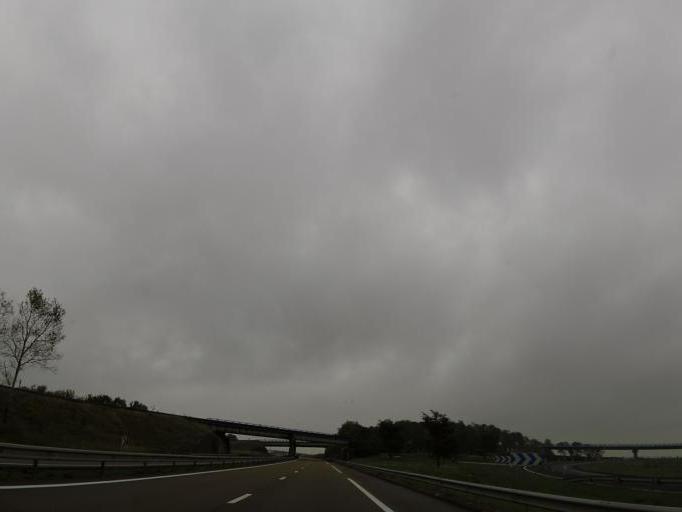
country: FR
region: Champagne-Ardenne
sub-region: Departement de la Marne
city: Fagnieres
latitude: 49.0568
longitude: 4.2853
